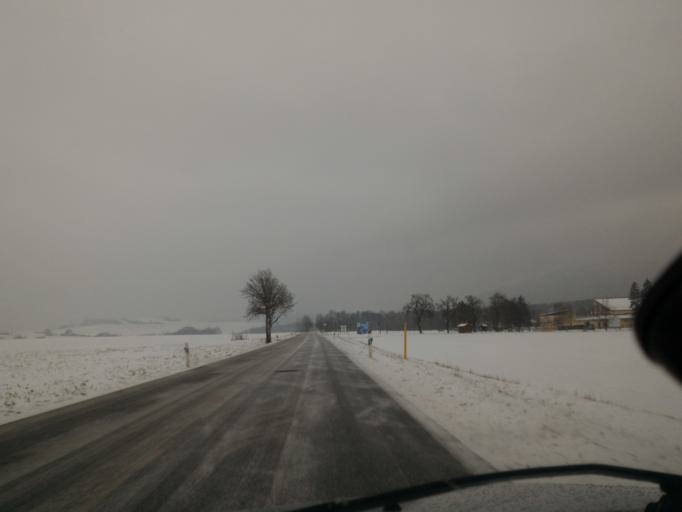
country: DE
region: Saxony
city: Grossschonau
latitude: 50.8836
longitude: 14.6695
